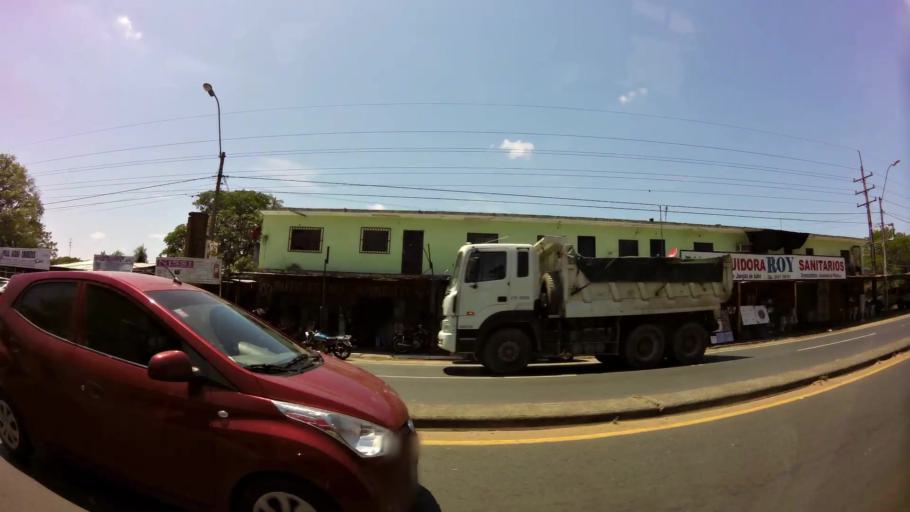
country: PY
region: Central
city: Nemby
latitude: -25.4026
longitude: -57.5432
